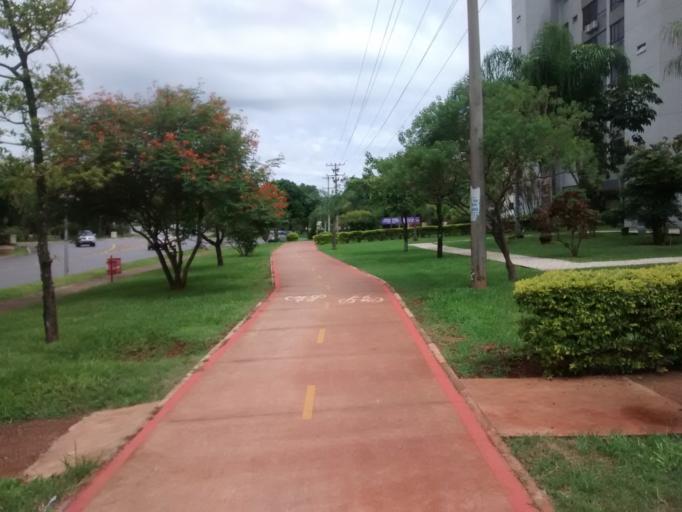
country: BR
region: Federal District
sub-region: Brasilia
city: Brasilia
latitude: -15.7546
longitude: -47.8900
